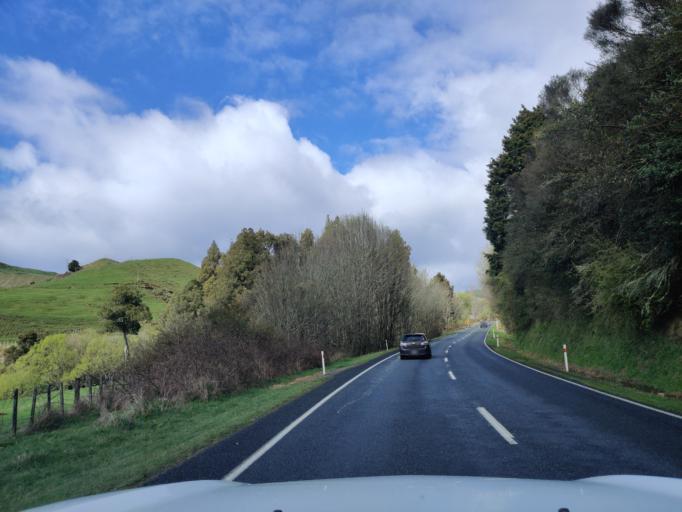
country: NZ
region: Waikato
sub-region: Otorohanga District
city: Otorohanga
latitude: -38.5943
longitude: 175.2196
